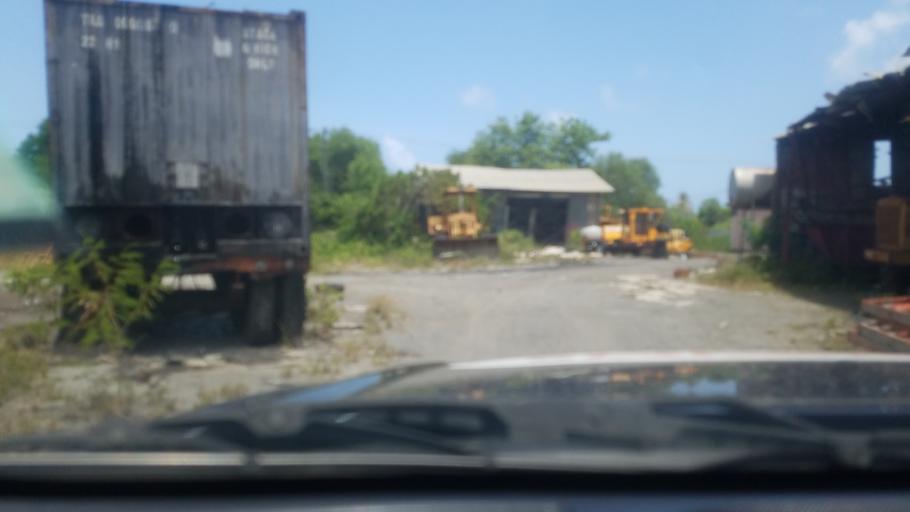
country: LC
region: Vieux-Fort
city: Vieux Fort
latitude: 13.7447
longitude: -60.9453
